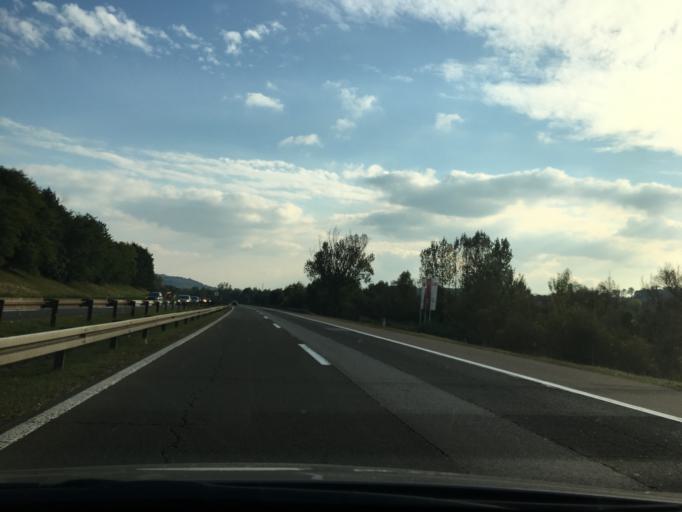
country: RS
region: Central Serbia
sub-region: Belgrade
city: Zvezdara
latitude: 44.6884
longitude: 20.5843
